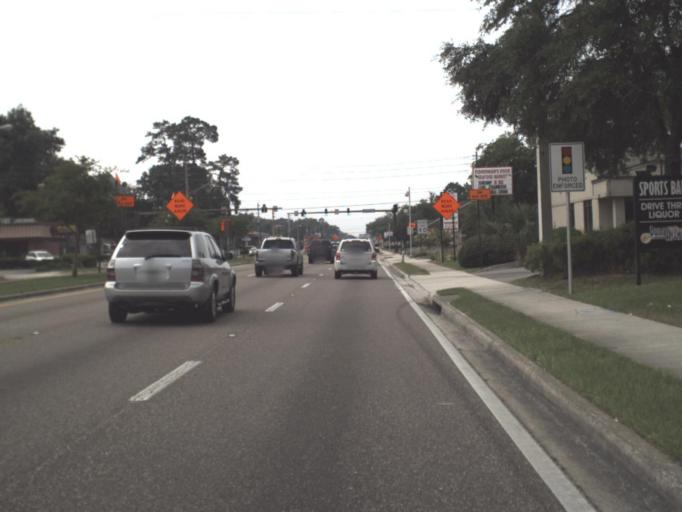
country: US
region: Florida
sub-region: Clay County
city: Orange Park
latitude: 30.1817
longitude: -81.7018
